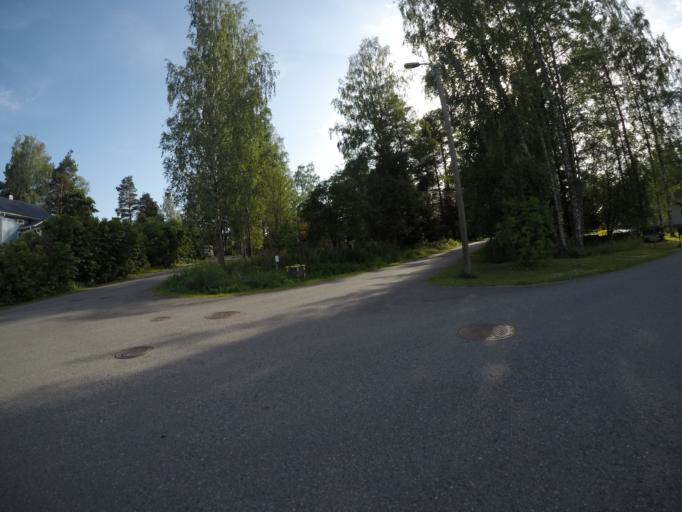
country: FI
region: Haeme
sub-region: Haemeenlinna
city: Haemeenlinna
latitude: 60.9809
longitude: 24.4197
